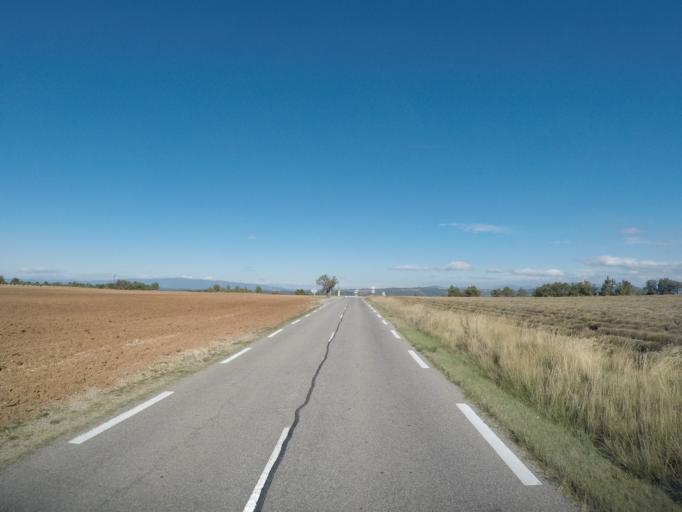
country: FR
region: Provence-Alpes-Cote d'Azur
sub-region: Departement des Alpes-de-Haute-Provence
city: Riez
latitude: 43.8947
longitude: 6.1296
